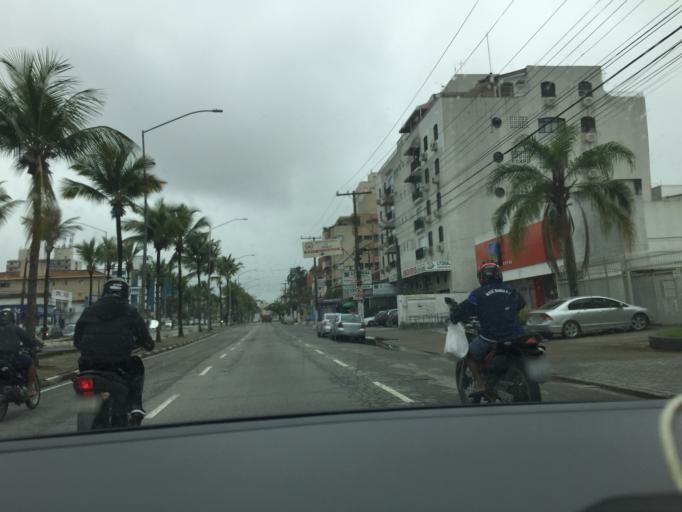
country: BR
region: Sao Paulo
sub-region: Guaruja
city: Guaruja
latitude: -23.9837
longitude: -46.2373
